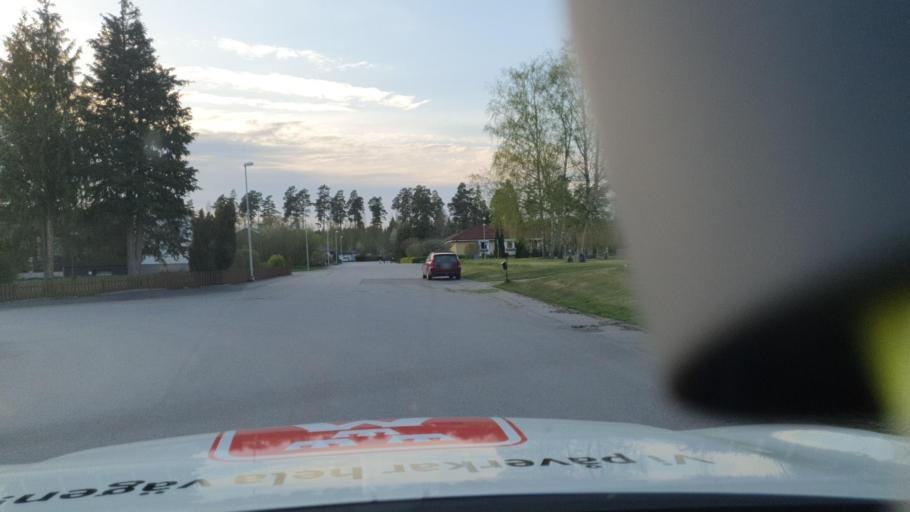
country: SE
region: OEstergoetland
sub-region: Linkopings Kommun
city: Vikingstad
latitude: 58.3848
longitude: 15.4259
